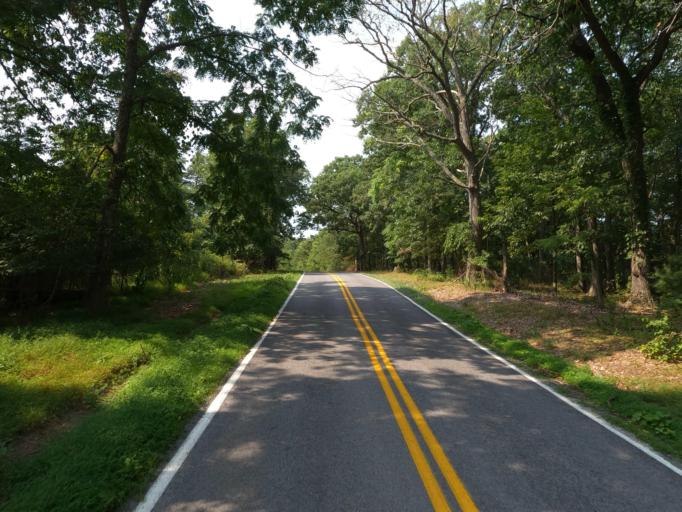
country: US
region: West Virginia
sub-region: Morgan County
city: Berkeley Springs
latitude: 39.6441
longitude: -78.2974
